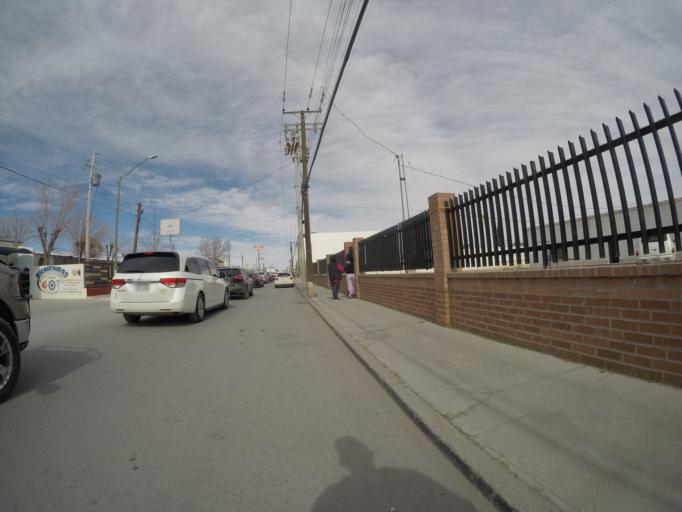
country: MX
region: Chihuahua
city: Ciudad Juarez
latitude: 31.7155
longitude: -106.4329
